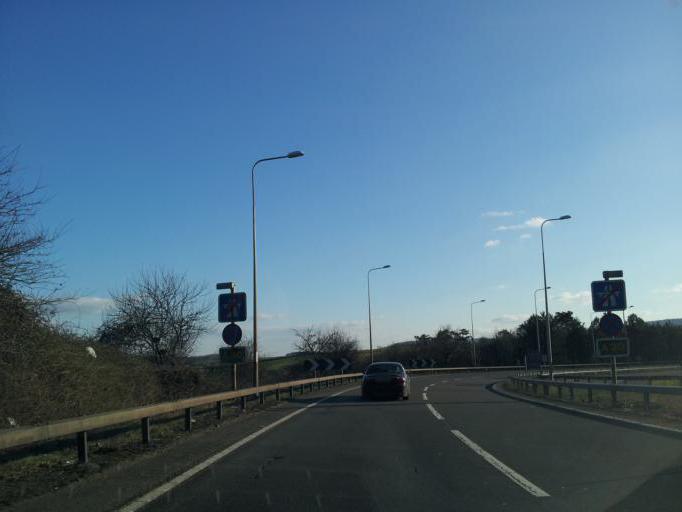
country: GB
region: England
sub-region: Devon
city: Exminster
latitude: 50.6798
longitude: -3.5138
